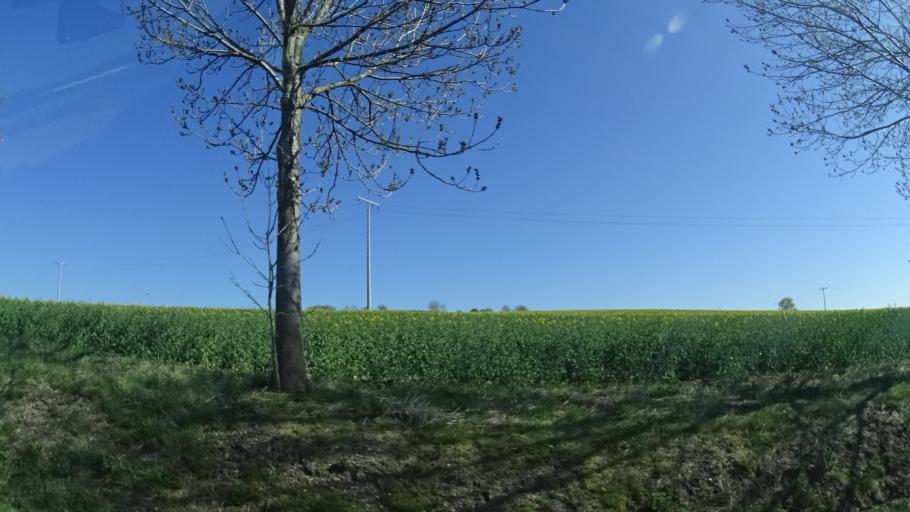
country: DE
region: Thuringia
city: Friedersdorf
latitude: 50.5949
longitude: 11.0368
